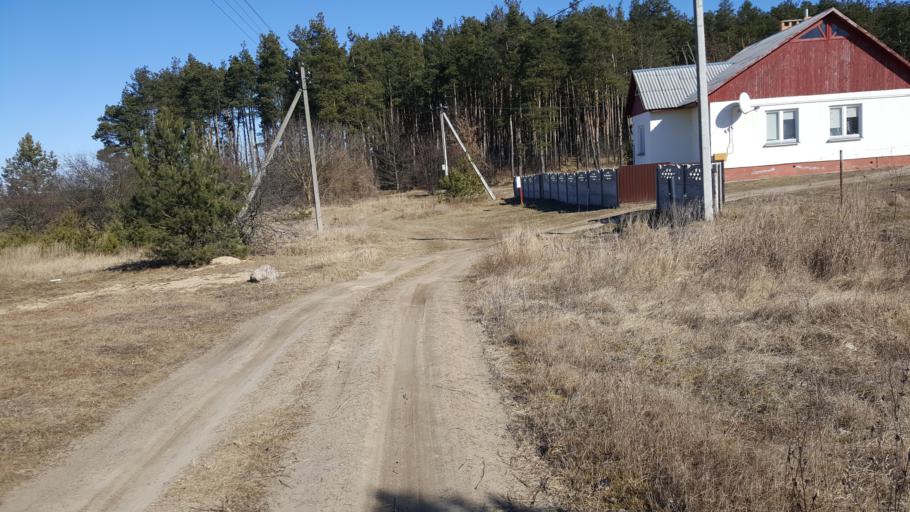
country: BY
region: Brest
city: Kamyanyets
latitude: 52.4073
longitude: 23.8377
